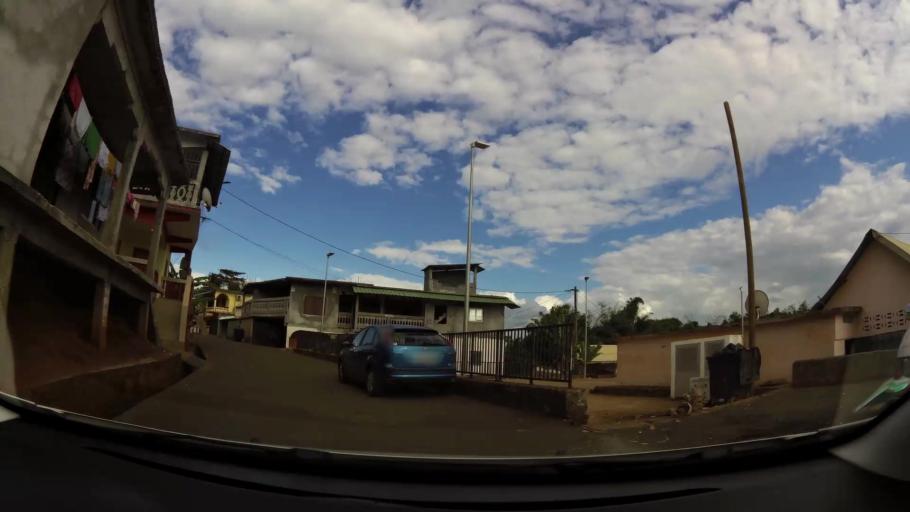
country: YT
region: Ouangani
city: Ouangani
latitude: -12.8375
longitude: 45.1299
